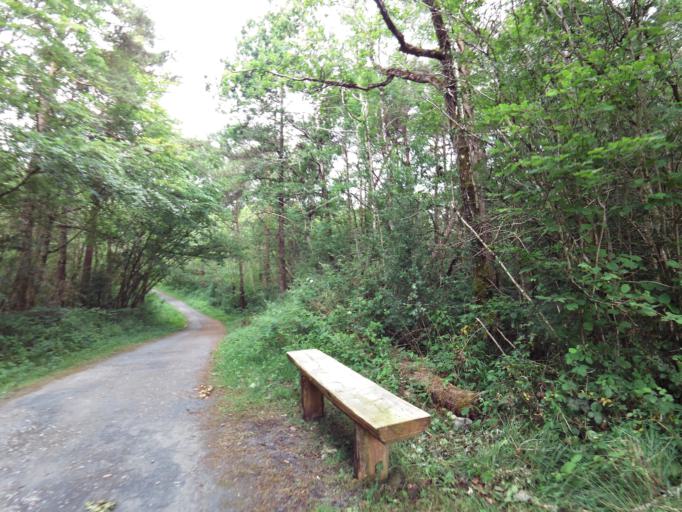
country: IE
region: Connaught
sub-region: County Galway
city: Gort
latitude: 53.0784
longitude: -8.8622
